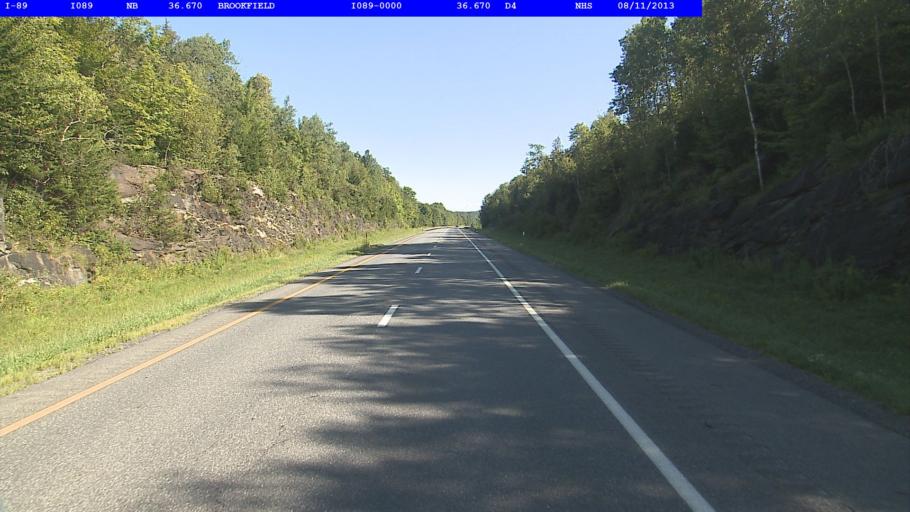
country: US
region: Vermont
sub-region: Orange County
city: Randolph
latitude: 44.0271
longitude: -72.6155
